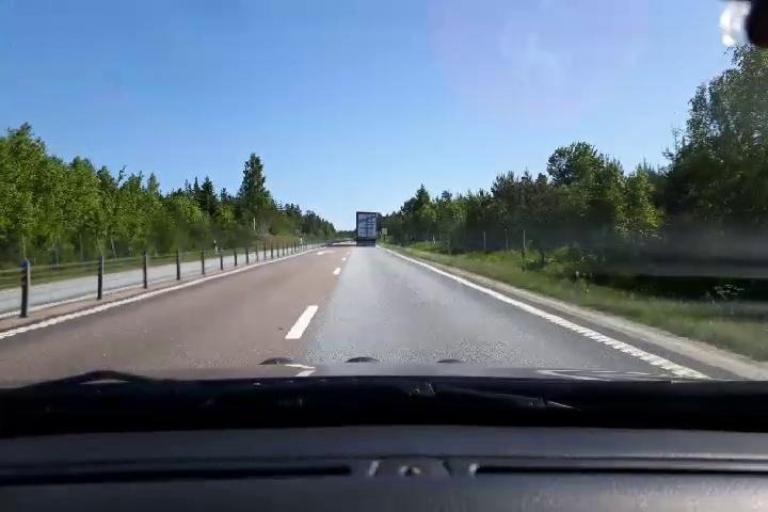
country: SE
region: Gaevleborg
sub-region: Soderhamns Kommun
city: Soderhamn
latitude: 61.2666
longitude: 17.0293
